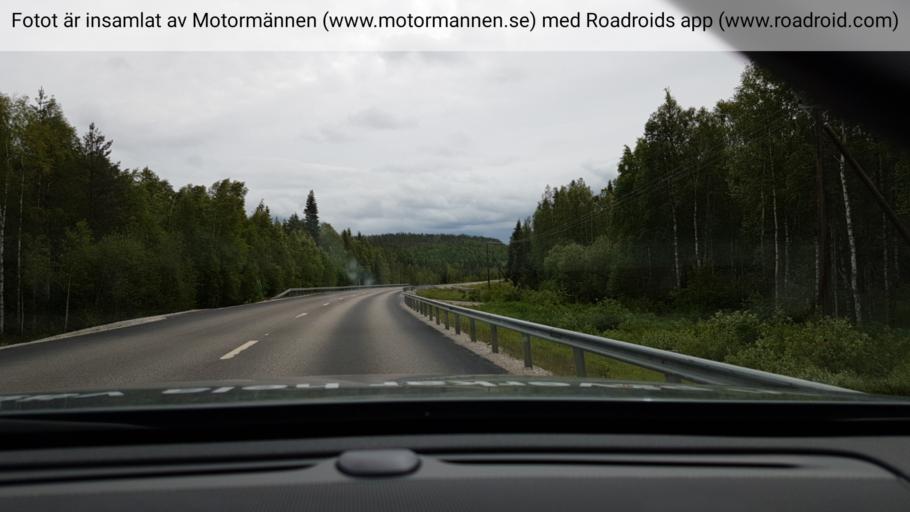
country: SE
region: Vaesterbotten
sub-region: Vannas Kommun
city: Vaennaes
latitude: 64.0454
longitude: 19.6848
